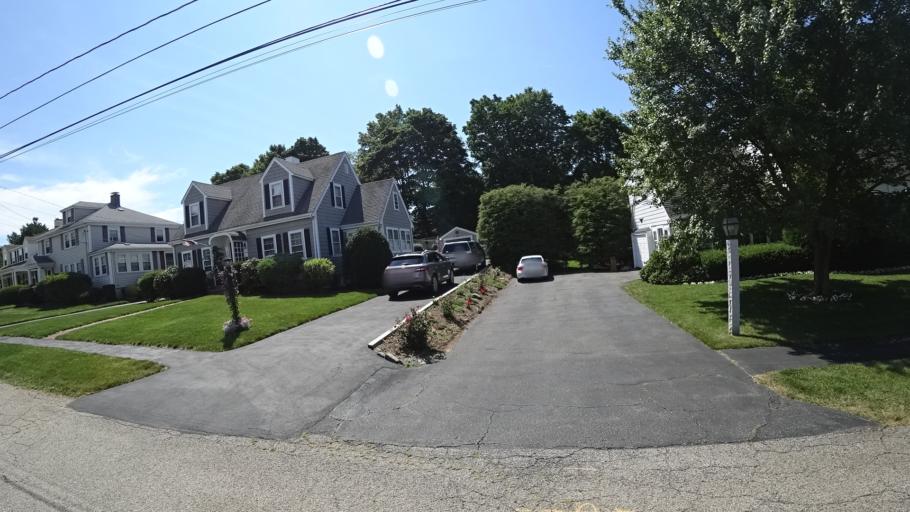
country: US
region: Massachusetts
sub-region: Norfolk County
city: Dedham
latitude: 42.2367
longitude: -71.1647
